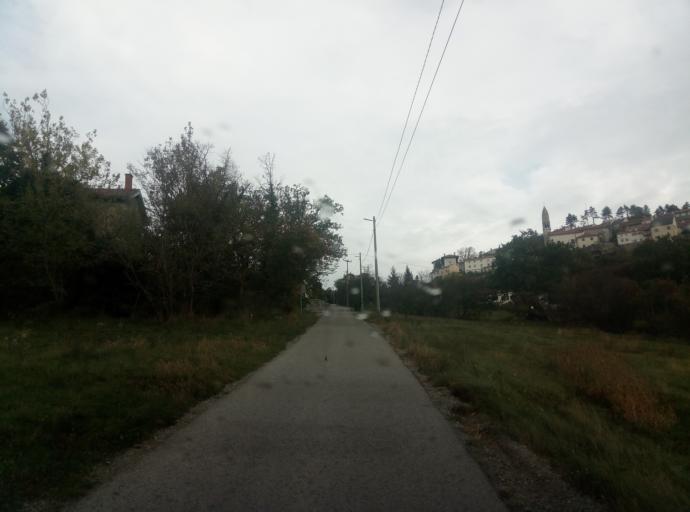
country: SI
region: Ajdovscina
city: Lokavec
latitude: 45.8209
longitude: 13.8454
